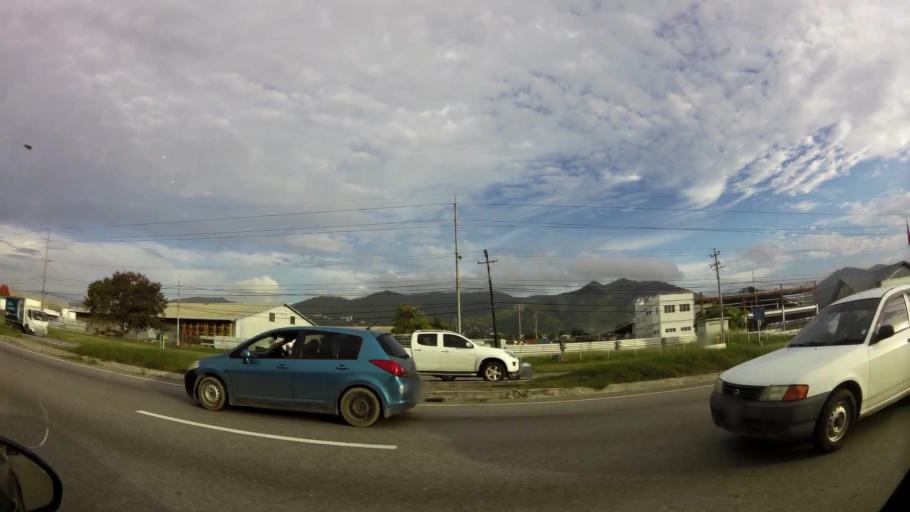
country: TT
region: Tunapuna/Piarco
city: Tunapuna
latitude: 10.6383
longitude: -61.3846
